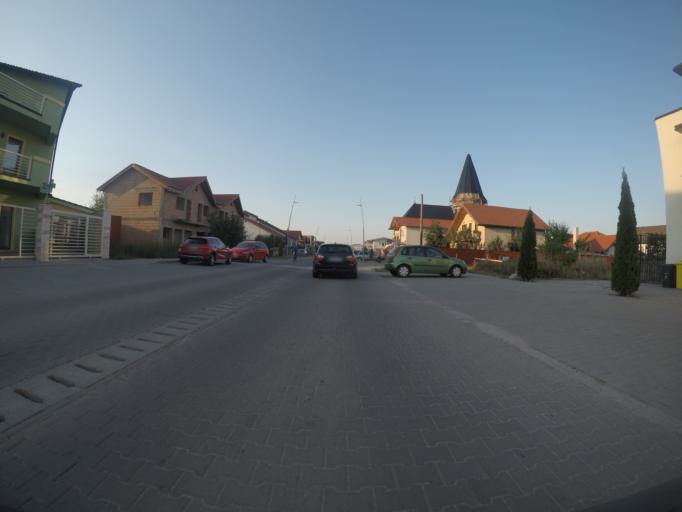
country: RO
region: Sibiu
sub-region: Comuna Selimbar
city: Selimbar
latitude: 45.7776
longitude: 24.1809
